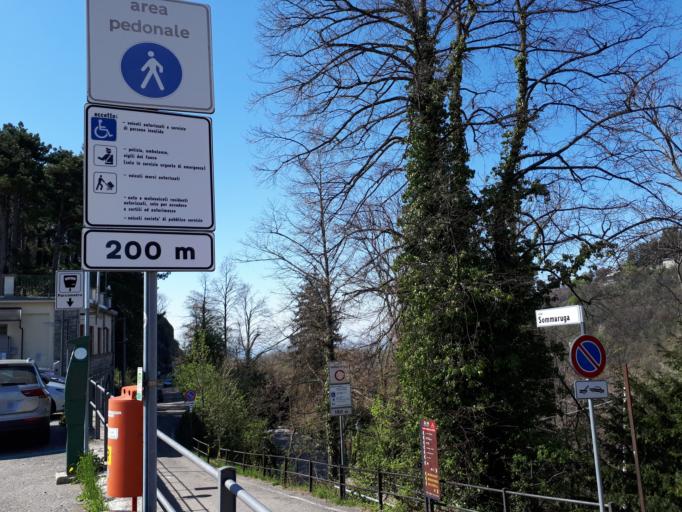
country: IT
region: Lombardy
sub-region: Provincia di Varese
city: Brinzio
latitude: 45.8633
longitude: 8.7919
